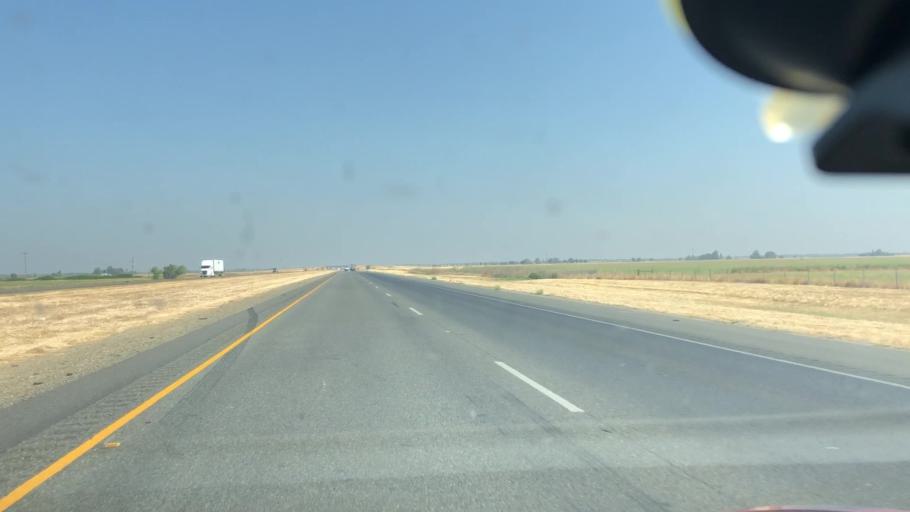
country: US
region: California
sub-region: Sacramento County
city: Laguna
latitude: 38.3572
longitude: -121.4726
